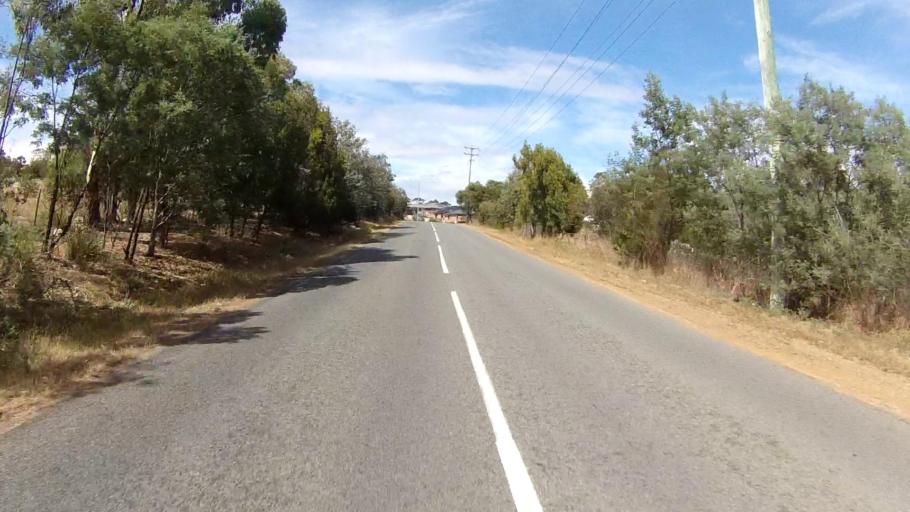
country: AU
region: Tasmania
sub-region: Clarence
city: Lindisfarne
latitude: -42.8194
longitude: 147.3512
